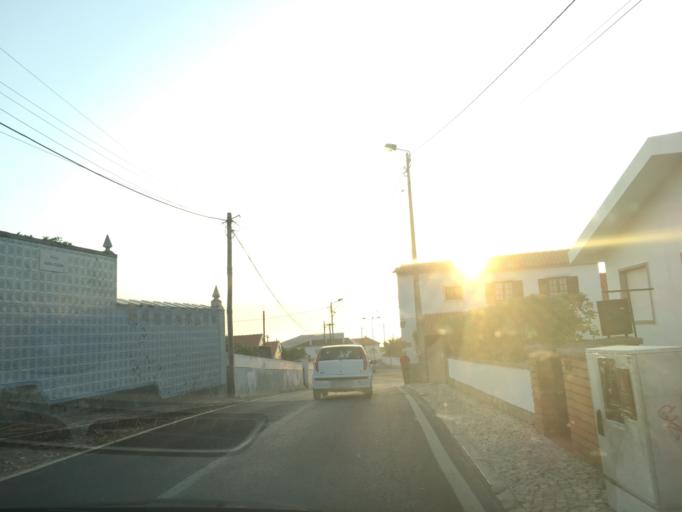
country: PT
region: Lisbon
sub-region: Sintra
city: Colares
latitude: 38.8382
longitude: -9.4606
